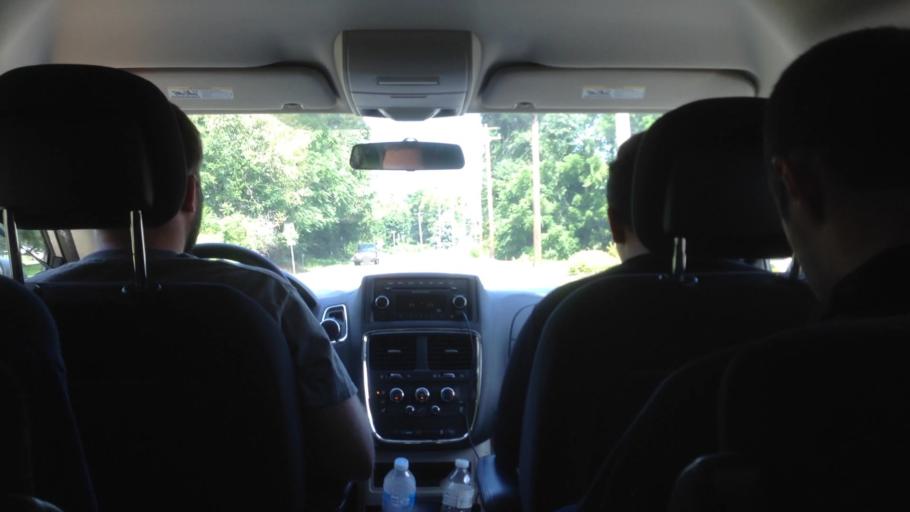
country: US
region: New York
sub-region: Dutchess County
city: Red Hook
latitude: 42.0297
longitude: -73.8471
